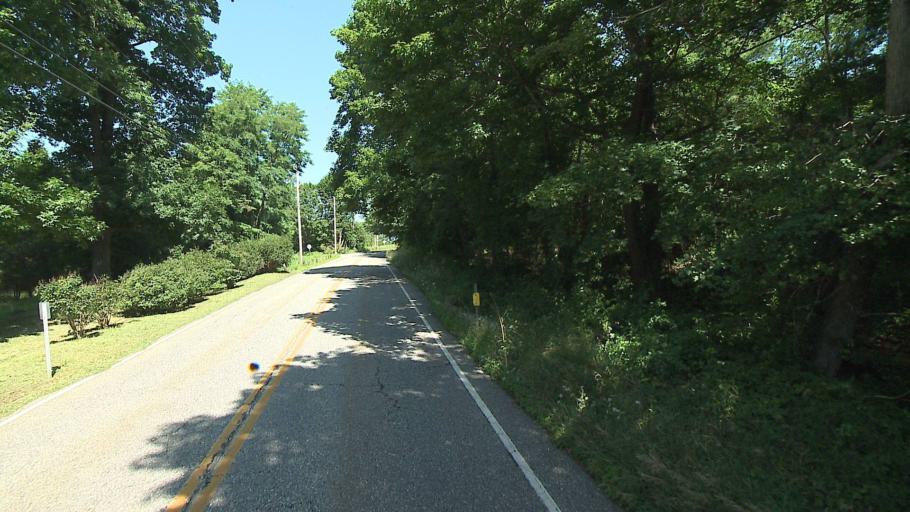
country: US
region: New York
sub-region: Dutchess County
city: Pine Plains
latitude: 41.9060
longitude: -73.4920
